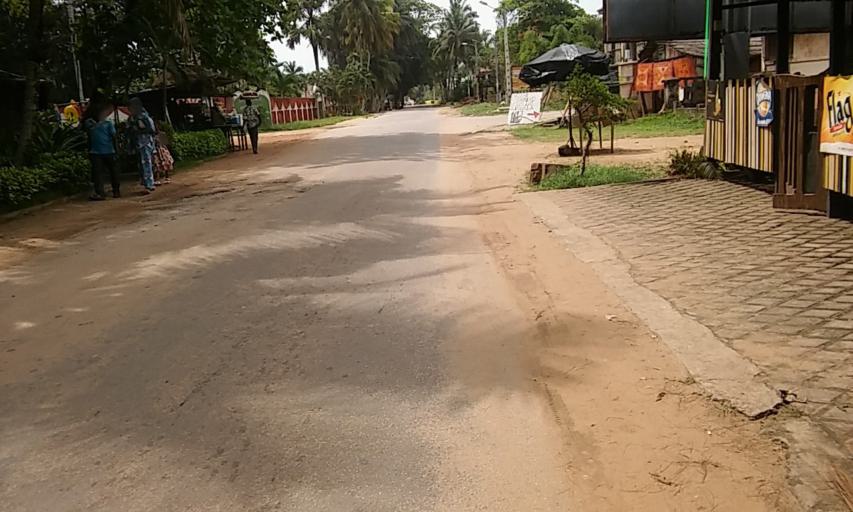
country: CI
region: Sud-Comoe
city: Grand-Bassam
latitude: 5.1960
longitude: -3.7388
